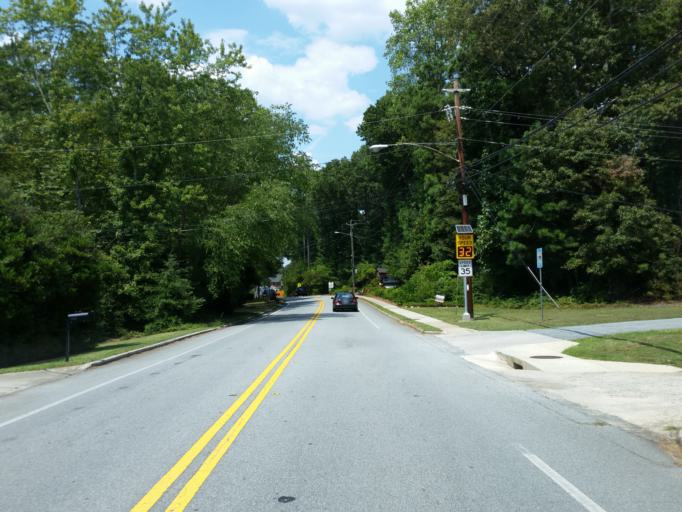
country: US
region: Georgia
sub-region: DeKalb County
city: Dunwoody
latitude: 33.9560
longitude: -84.3362
